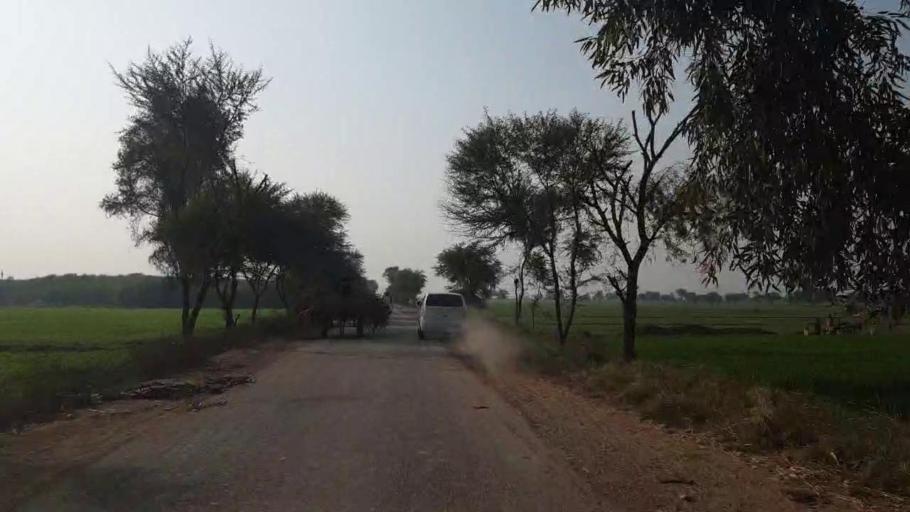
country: PK
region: Sindh
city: Shahdadpur
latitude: 25.9713
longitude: 68.5346
